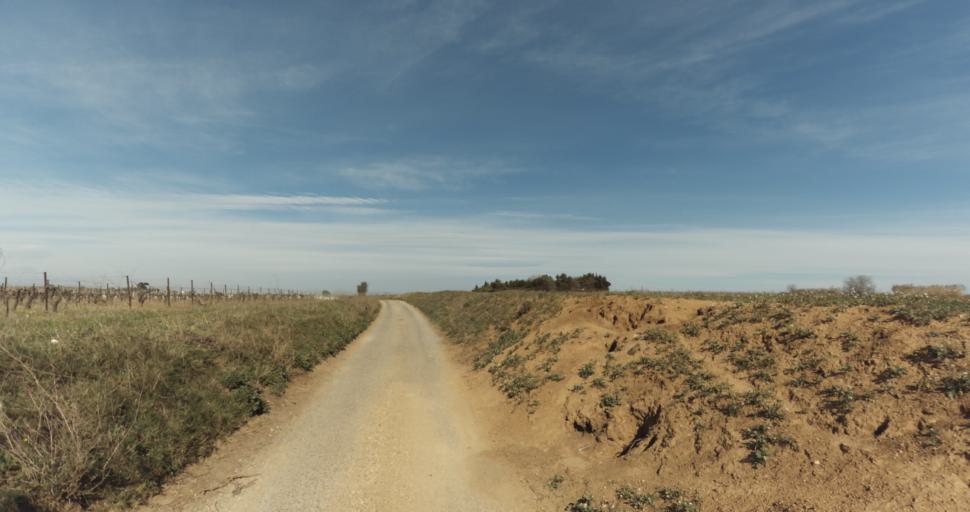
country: FR
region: Languedoc-Roussillon
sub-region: Departement de l'Herault
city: Marseillan
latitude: 43.3488
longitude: 3.5024
